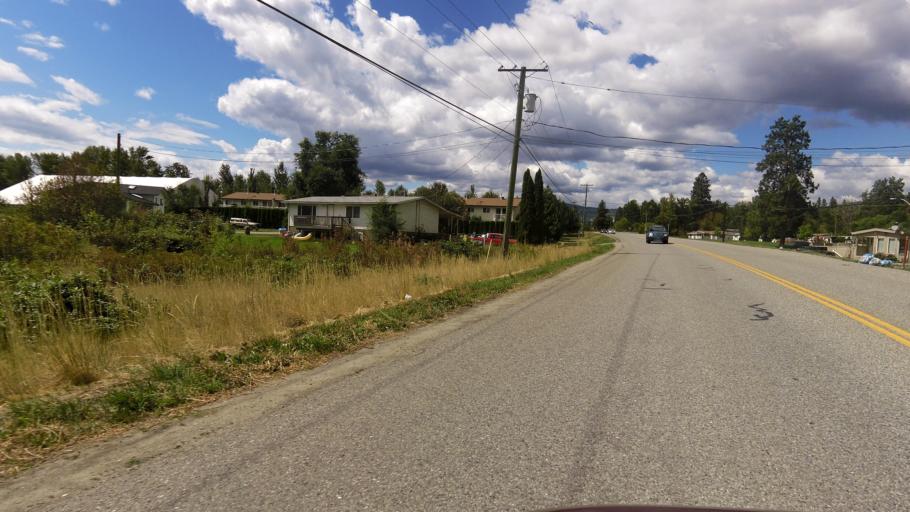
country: CA
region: British Columbia
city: West Kelowna
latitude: 49.8314
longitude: -119.5917
